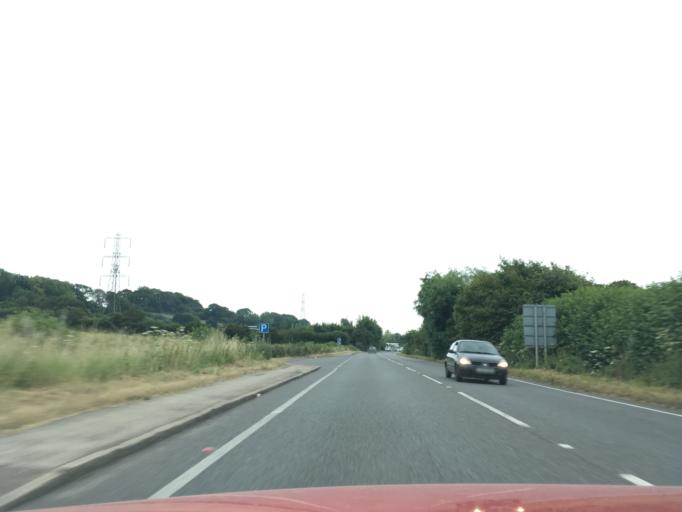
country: GB
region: England
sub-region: Central Bedfordshire
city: Kensworth
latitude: 51.8632
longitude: -0.4848
